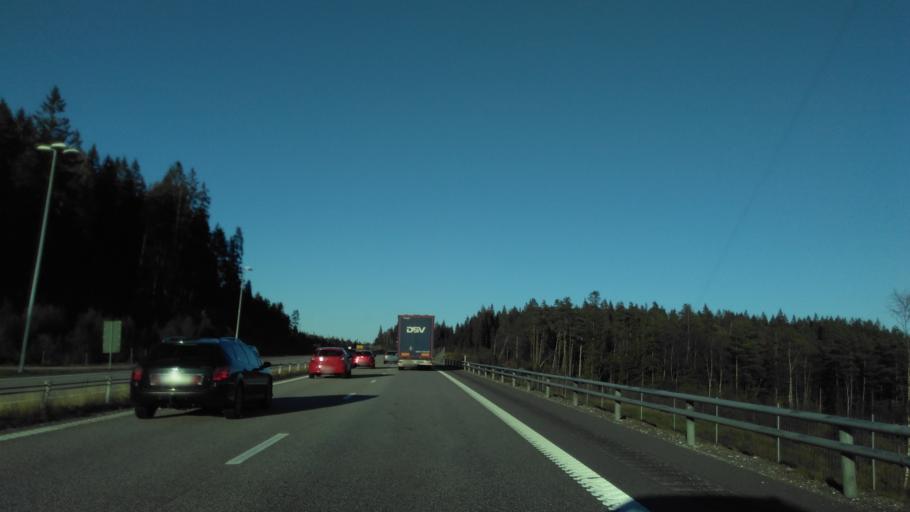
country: SE
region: Vaestra Goetaland
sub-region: Boras Kommun
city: Dalsjofors
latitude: 57.7440
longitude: 13.0635
